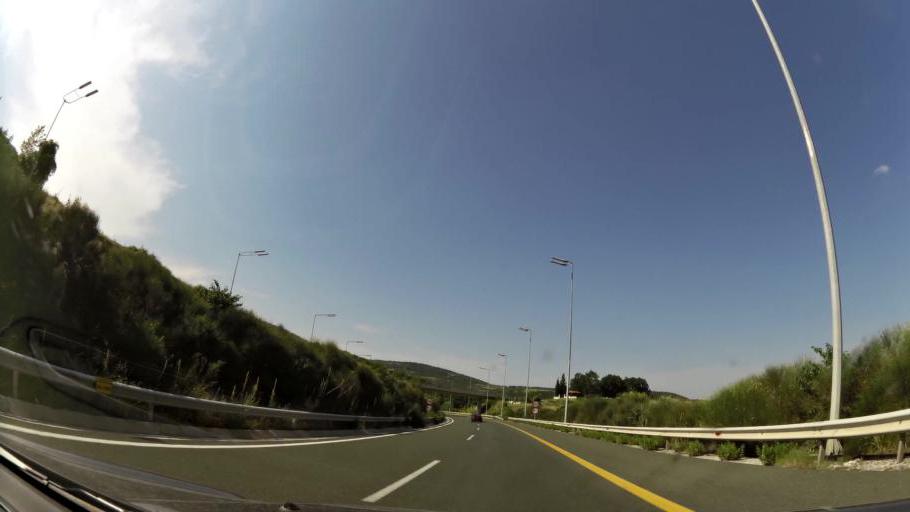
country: GR
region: Central Macedonia
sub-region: Nomos Imathias
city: Rizomata
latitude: 40.4286
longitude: 22.1834
